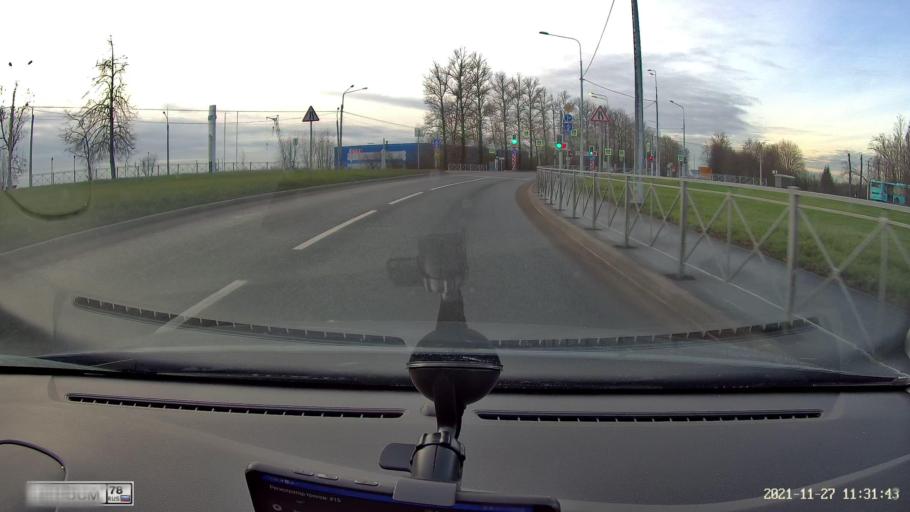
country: RU
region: St.-Petersburg
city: Krasnoye Selo
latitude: 59.7172
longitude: 30.0467
